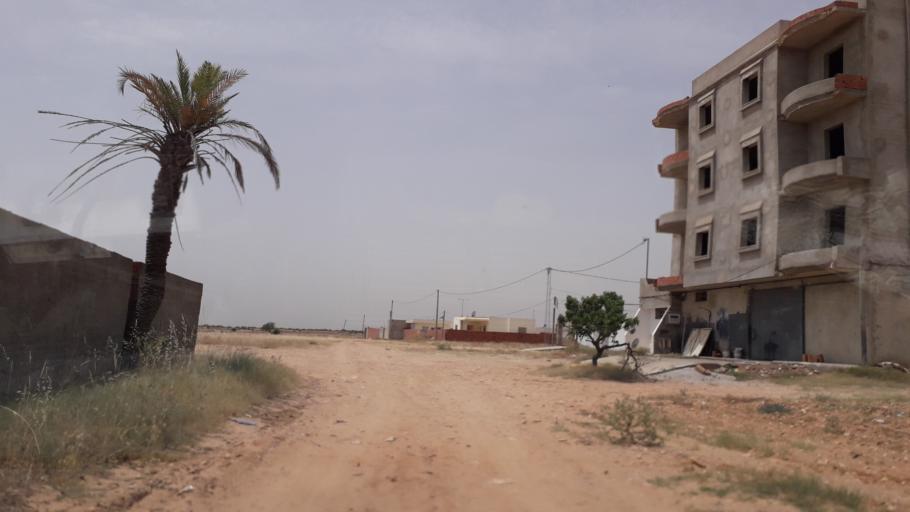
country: TN
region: Safaqis
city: Al Qarmadah
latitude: 34.8484
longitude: 10.7587
